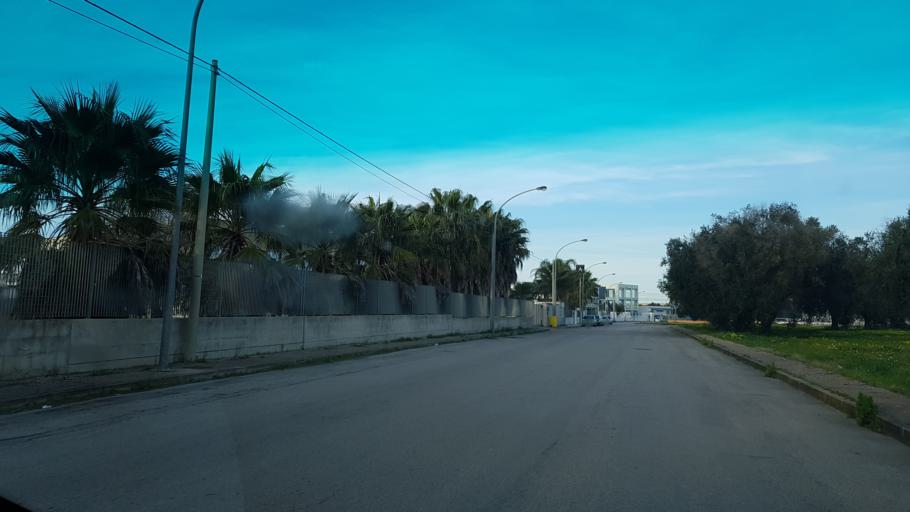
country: IT
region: Apulia
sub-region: Provincia di Brindisi
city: Mesagne
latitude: 40.5755
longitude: 17.8306
